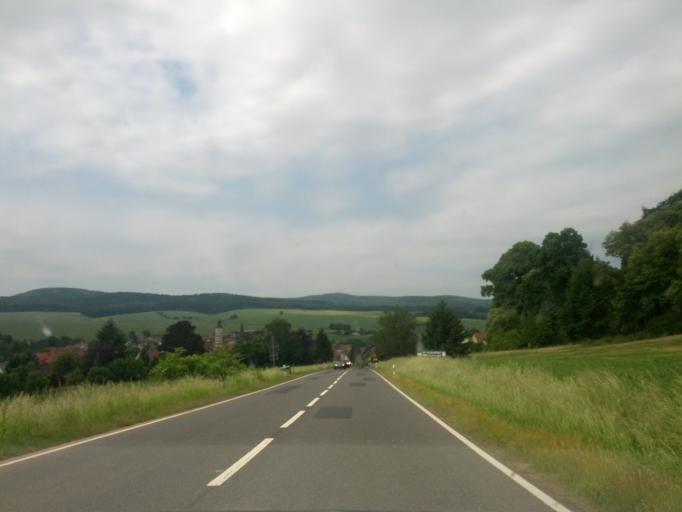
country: DE
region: Thuringia
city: Marksuhl
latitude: 50.9169
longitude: 10.2094
